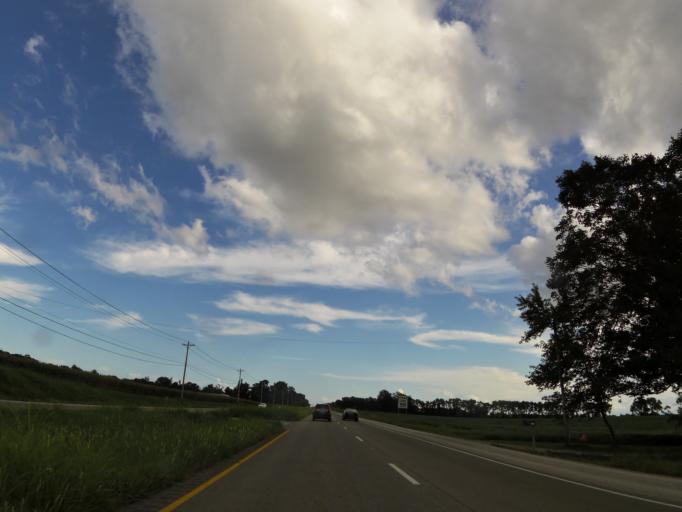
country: US
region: Kentucky
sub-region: Christian County
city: Oak Grove
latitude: 36.7498
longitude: -87.4686
